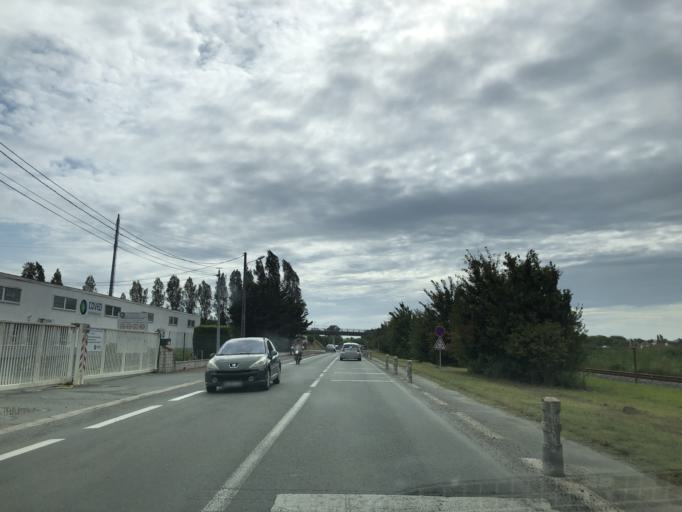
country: FR
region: Poitou-Charentes
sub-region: Departement de la Charente-Maritime
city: Royan
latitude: 45.6315
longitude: -1.0038
